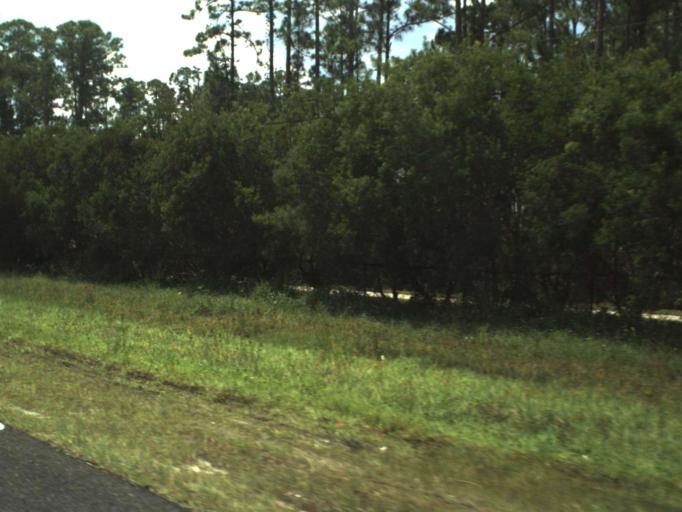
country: US
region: Florida
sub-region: Volusia County
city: Glencoe
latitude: 29.0123
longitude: -81.0153
